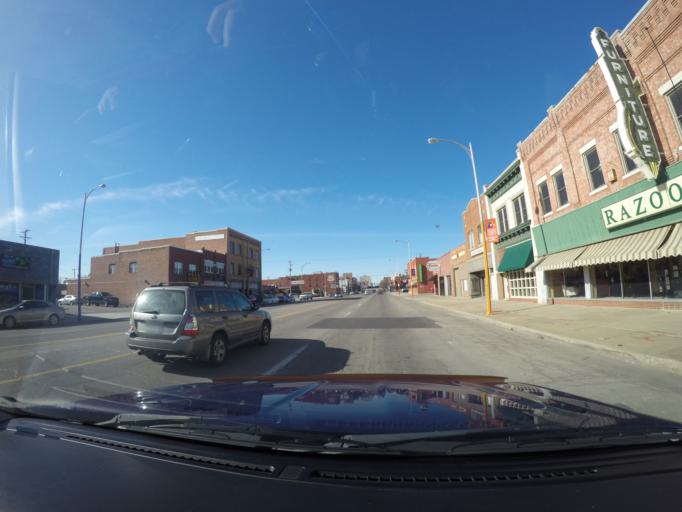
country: US
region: Kansas
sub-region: Sedgwick County
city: Wichita
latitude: 37.6861
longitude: -97.3241
